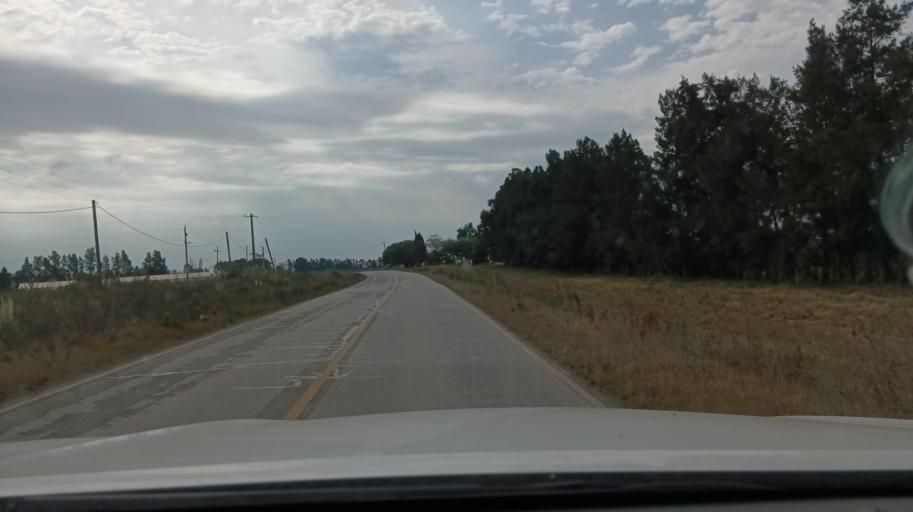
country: UY
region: Canelones
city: Sauce
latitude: -34.6454
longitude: -56.1063
